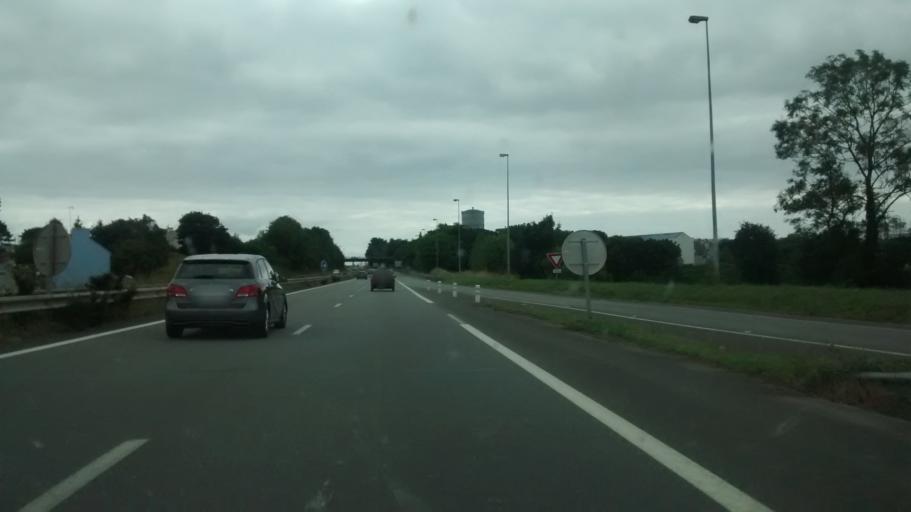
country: FR
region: Brittany
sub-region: Departement du Finistere
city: Brest
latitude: 48.4217
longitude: -4.4774
